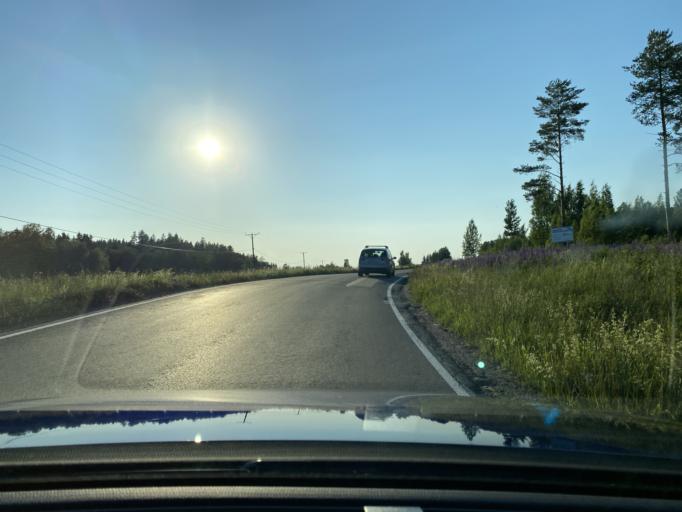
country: FI
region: Haeme
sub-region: Haemeenlinna
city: Tervakoski
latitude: 60.7299
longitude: 24.6747
